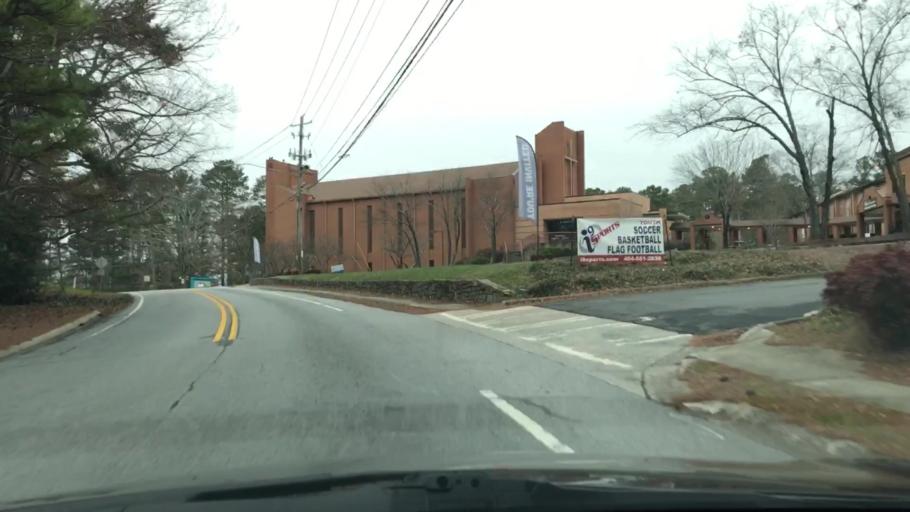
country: US
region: Georgia
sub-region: DeKalb County
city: Doraville
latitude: 33.9355
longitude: -84.2870
